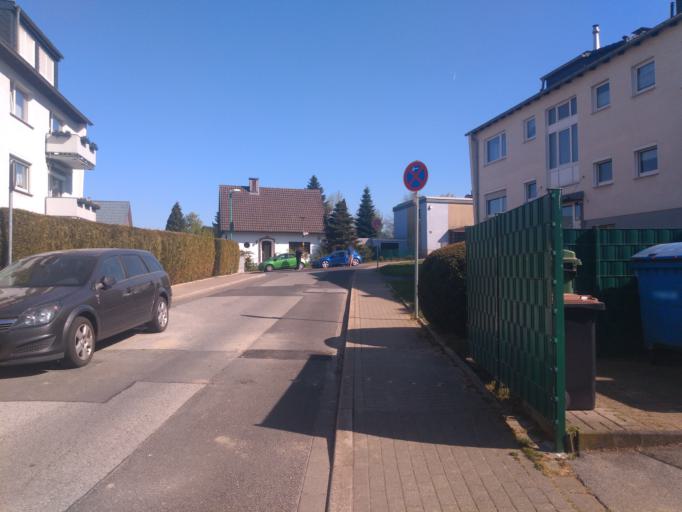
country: DE
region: North Rhine-Westphalia
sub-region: Regierungsbezirk Dusseldorf
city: Velbert
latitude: 51.3071
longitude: 7.1044
